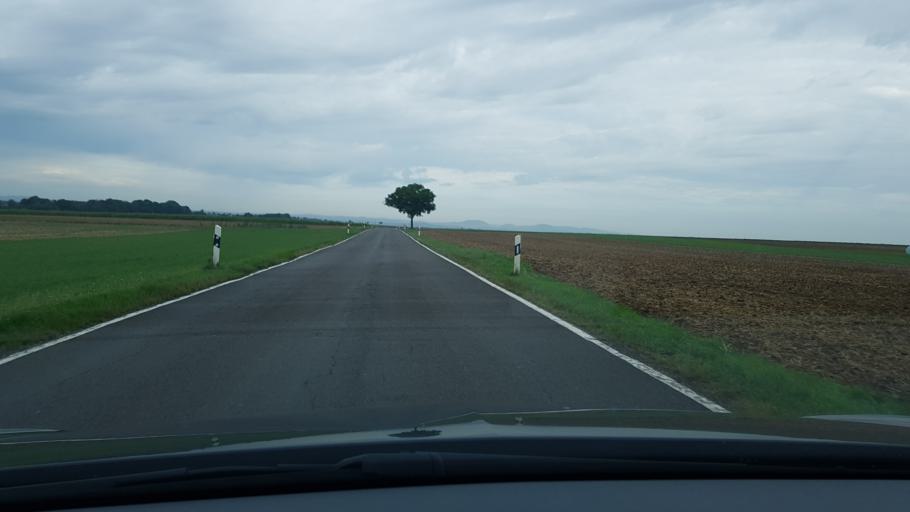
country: DE
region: Rheinland-Pfalz
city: Hatzenport
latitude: 50.2486
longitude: 7.4156
